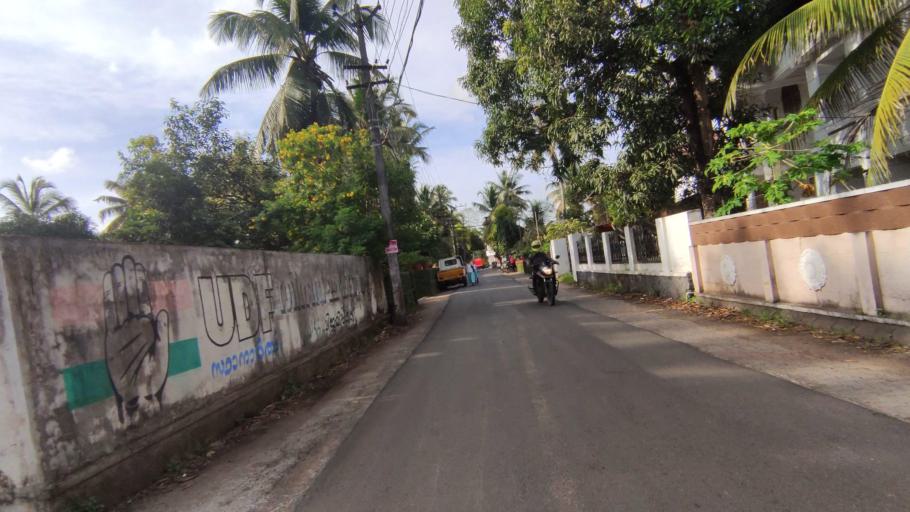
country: IN
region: Kerala
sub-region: Kottayam
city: Kottayam
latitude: 9.5840
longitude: 76.4989
